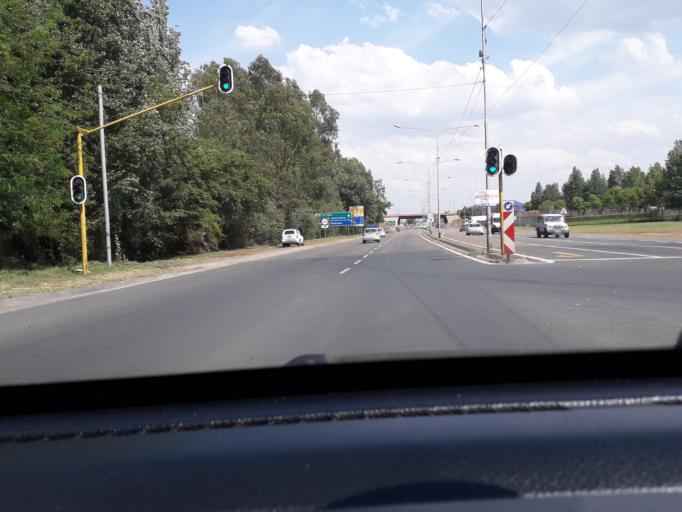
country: ZA
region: Gauteng
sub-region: City of Tshwane Metropolitan Municipality
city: Centurion
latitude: -25.8554
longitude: 28.2187
